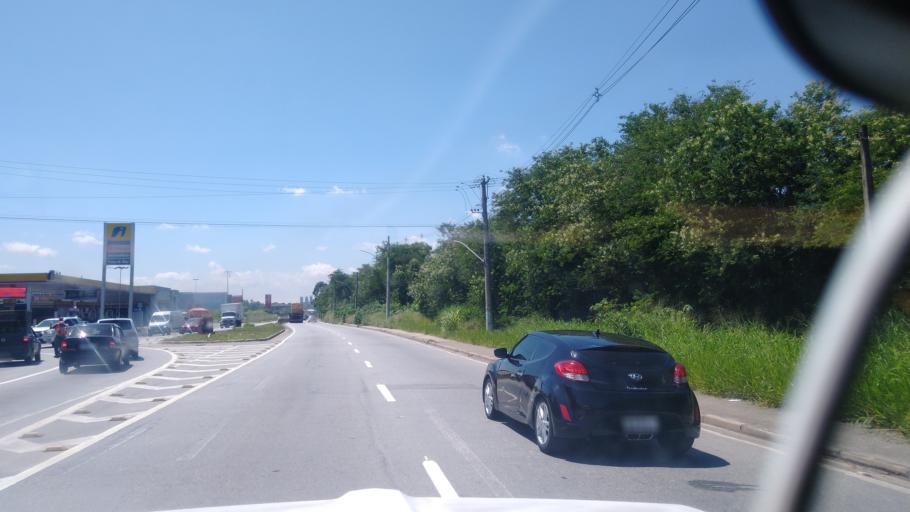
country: BR
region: Sao Paulo
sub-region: Itaquaquecetuba
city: Itaquaquecetuba
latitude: -23.4719
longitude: -46.3308
